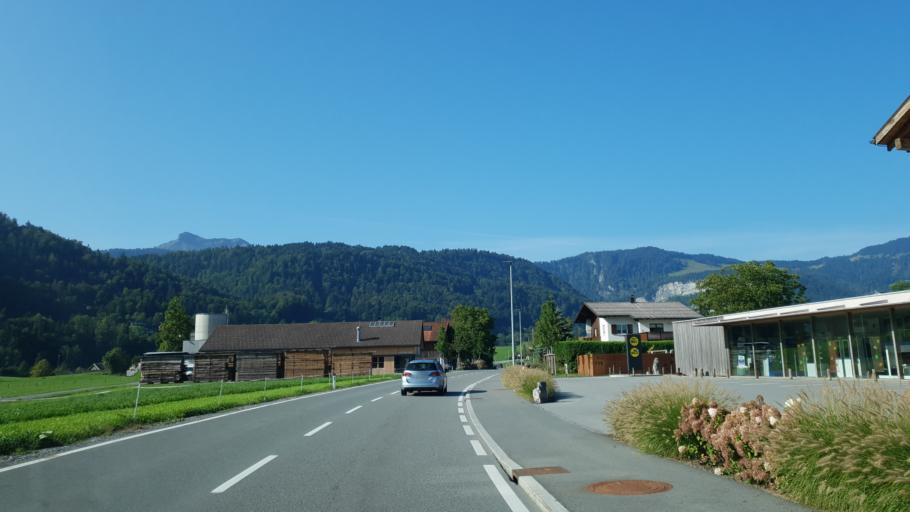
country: AT
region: Vorarlberg
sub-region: Politischer Bezirk Bregenz
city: Andelsbuch
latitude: 47.4074
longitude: 9.8882
